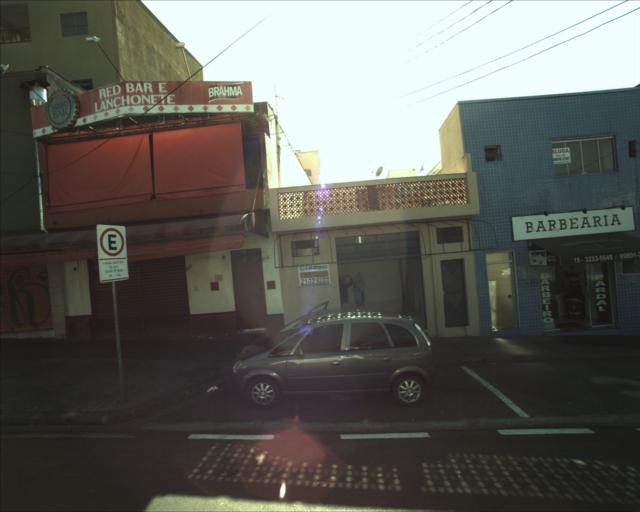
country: BR
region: Sao Paulo
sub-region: Sorocaba
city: Sorocaba
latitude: -23.4945
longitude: -47.4642
